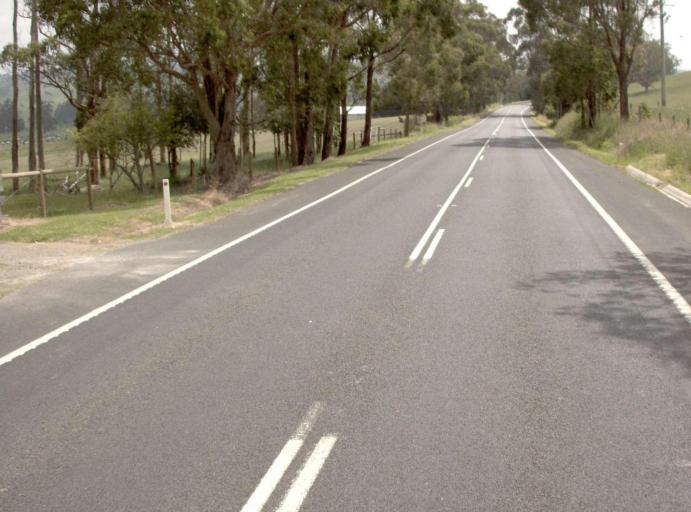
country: AU
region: Victoria
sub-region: Baw Baw
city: Warragul
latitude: -38.4158
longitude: 146.0439
